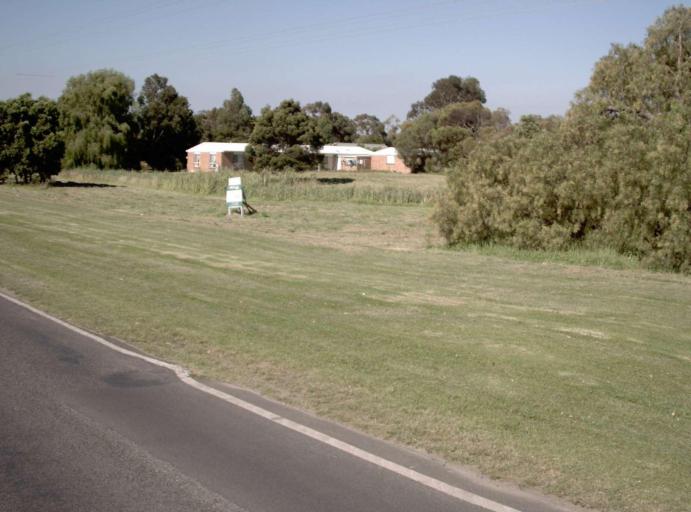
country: AU
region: Victoria
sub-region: Latrobe
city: Traralgon
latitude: -38.5722
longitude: 146.6740
